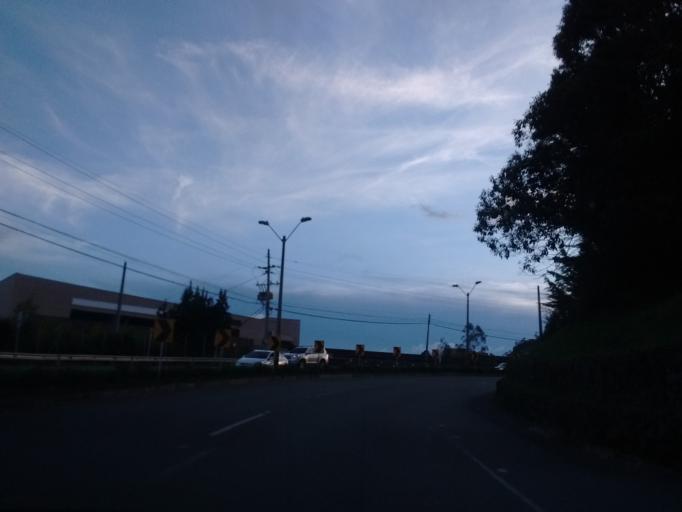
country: CO
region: Antioquia
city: Envigado
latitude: 6.1531
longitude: -75.5394
